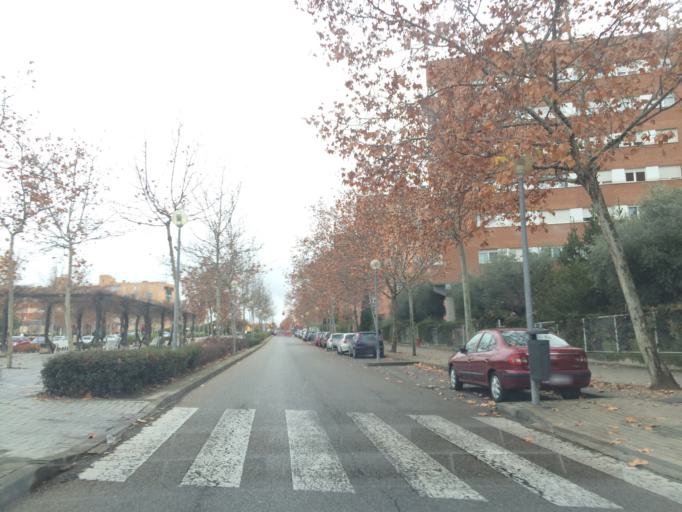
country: ES
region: Madrid
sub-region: Provincia de Madrid
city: Tres Cantos
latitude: 40.6018
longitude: -3.7138
